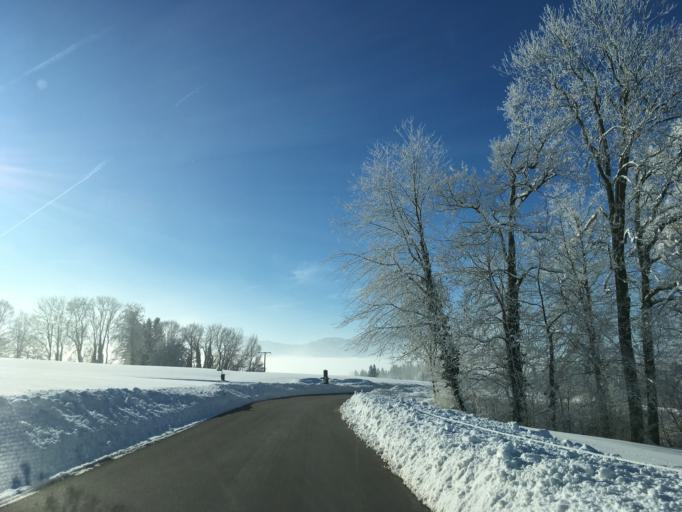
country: DE
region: Bavaria
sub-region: Upper Bavaria
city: Bad Endorf
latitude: 47.8685
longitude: 12.2890
